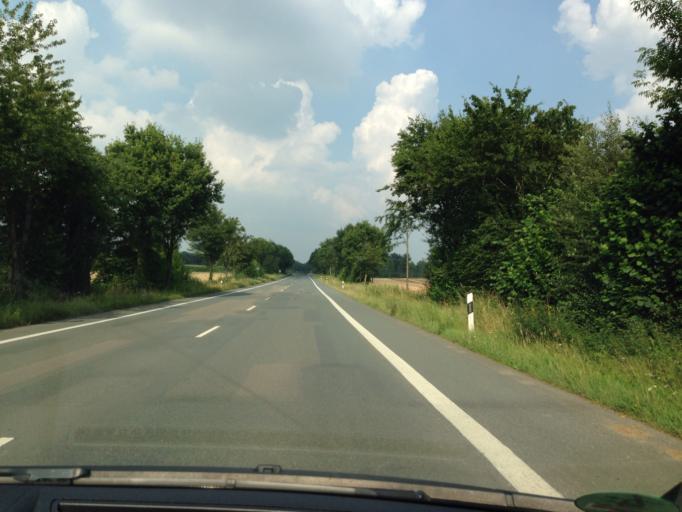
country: DE
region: North Rhine-Westphalia
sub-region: Regierungsbezirk Munster
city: Altenberge
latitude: 51.9783
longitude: 7.5234
